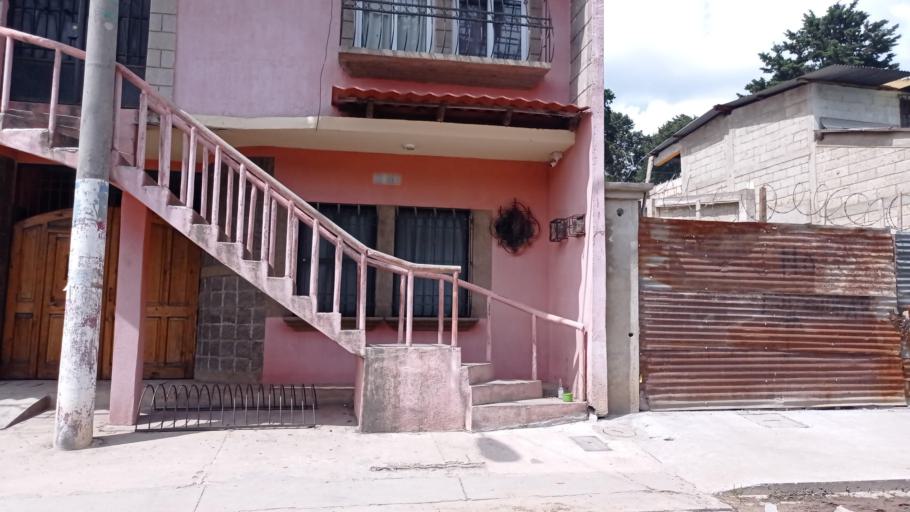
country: GT
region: Quetzaltenango
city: Quetzaltenango
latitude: 14.8440
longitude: -91.5027
